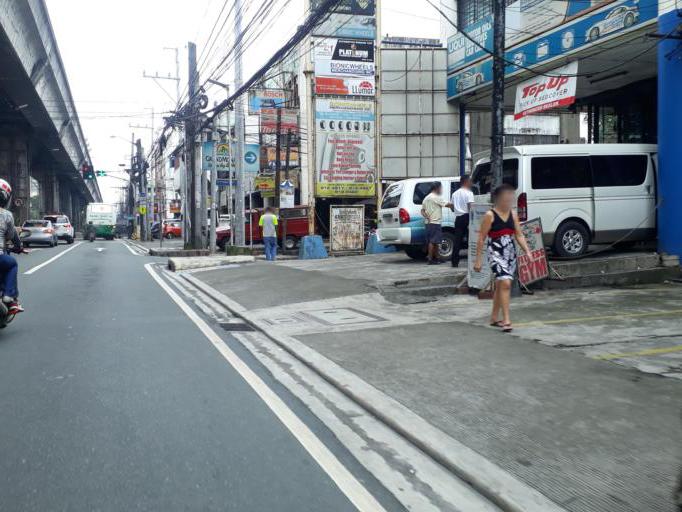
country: PH
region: Metro Manila
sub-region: Quezon City
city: Quezon City
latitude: 14.6269
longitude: 121.0611
